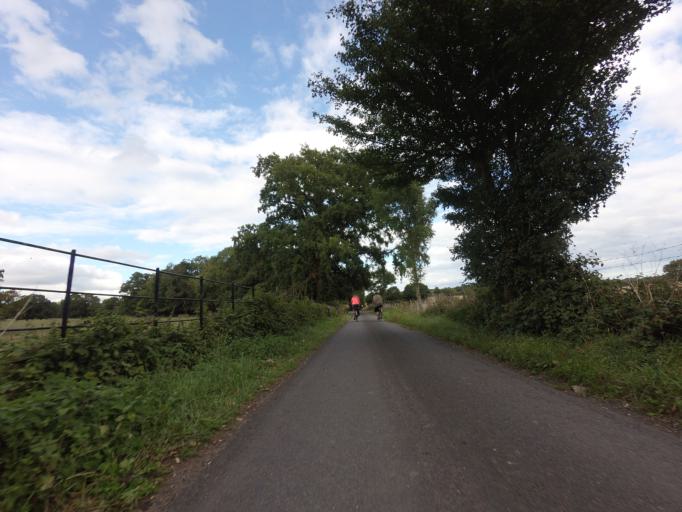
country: GB
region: England
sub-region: Kent
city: Marden
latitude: 51.2129
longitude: 0.5169
